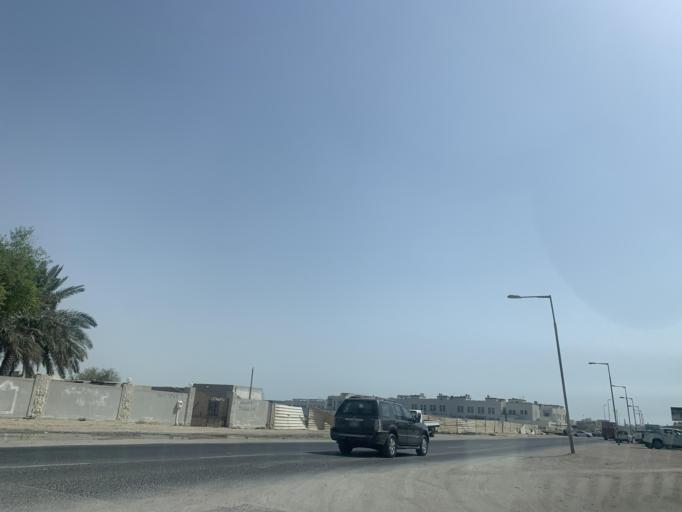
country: BH
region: Central Governorate
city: Madinat Hamad
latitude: 26.1361
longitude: 50.4842
